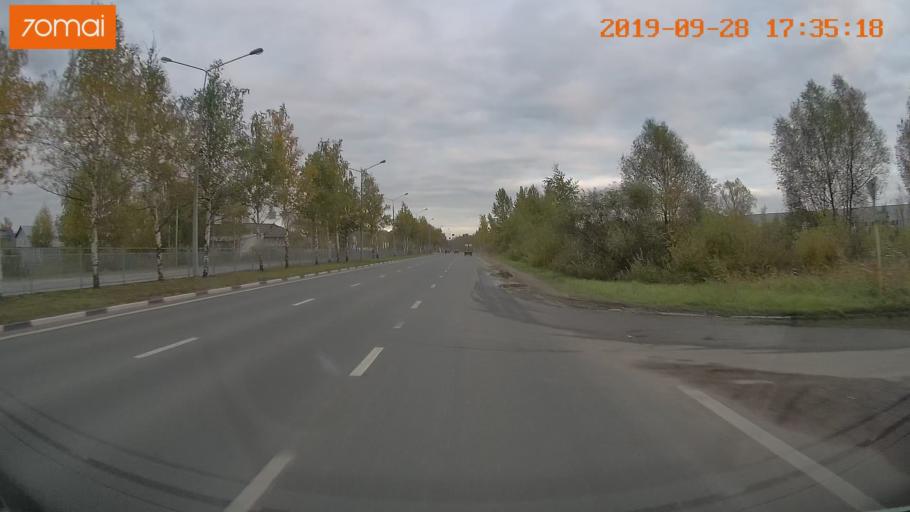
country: RU
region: Jaroslavl
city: Yaroslavl
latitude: 57.5514
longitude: 39.9502
